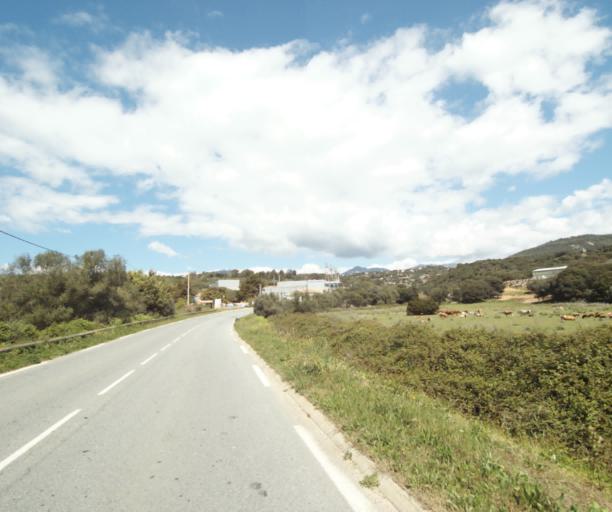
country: FR
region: Corsica
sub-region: Departement de la Corse-du-Sud
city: Propriano
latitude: 41.6597
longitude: 8.9170
